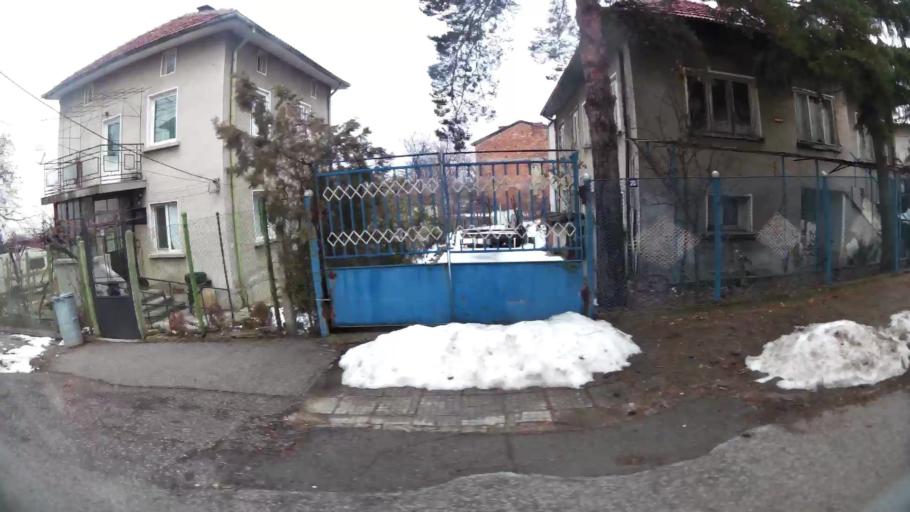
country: BG
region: Sofiya
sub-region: Obshtina Bozhurishte
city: Bozhurishte
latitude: 42.6807
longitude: 23.2359
